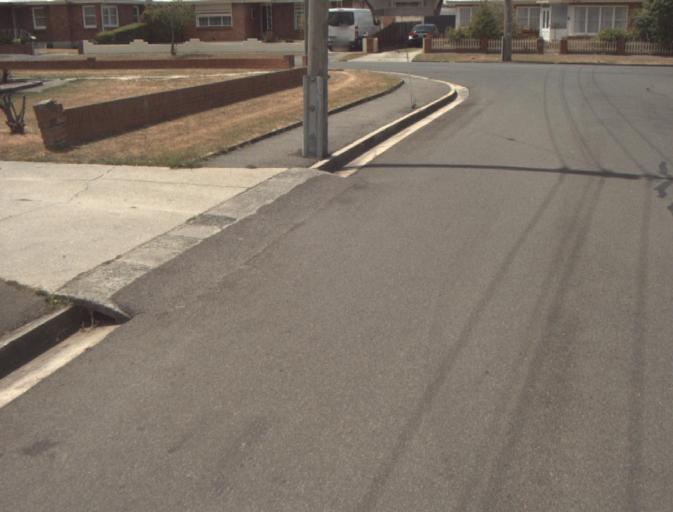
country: AU
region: Tasmania
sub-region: Launceston
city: Newnham
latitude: -41.4091
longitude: 147.1454
